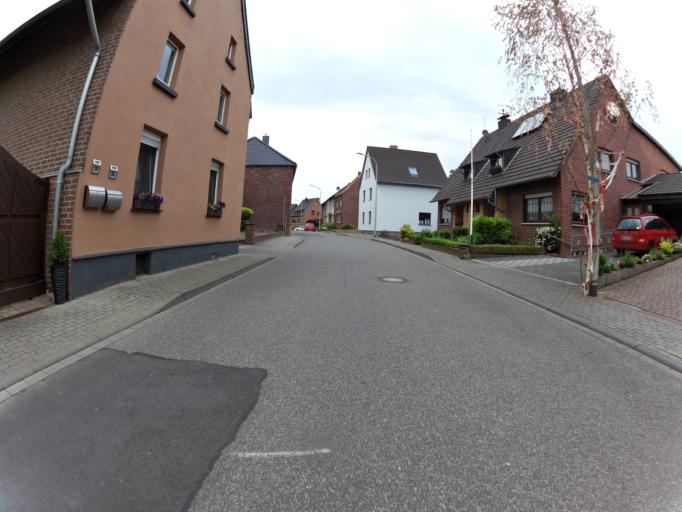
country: DE
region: North Rhine-Westphalia
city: Geilenkirchen
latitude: 50.9857
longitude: 6.1840
